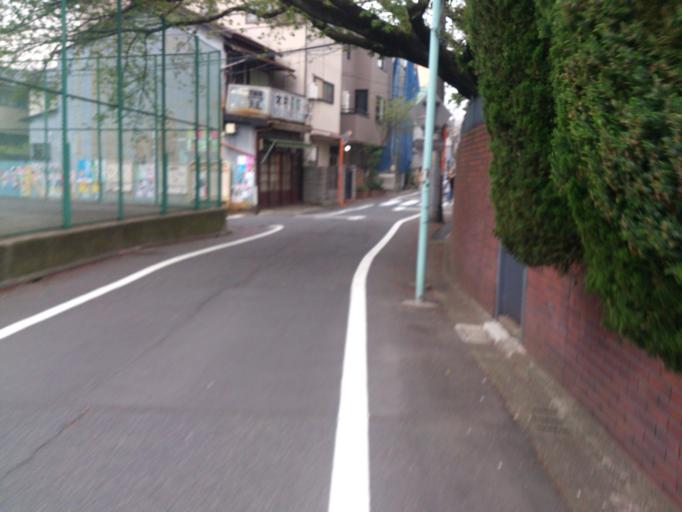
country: JP
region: Tokyo
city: Tokyo
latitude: 35.6632
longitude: 139.6747
